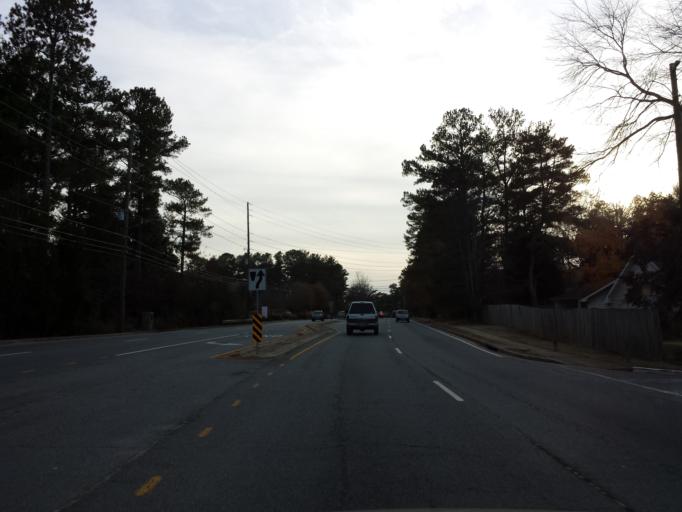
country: US
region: Georgia
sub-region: Fulton County
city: Roswell
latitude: 34.0084
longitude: -84.4335
